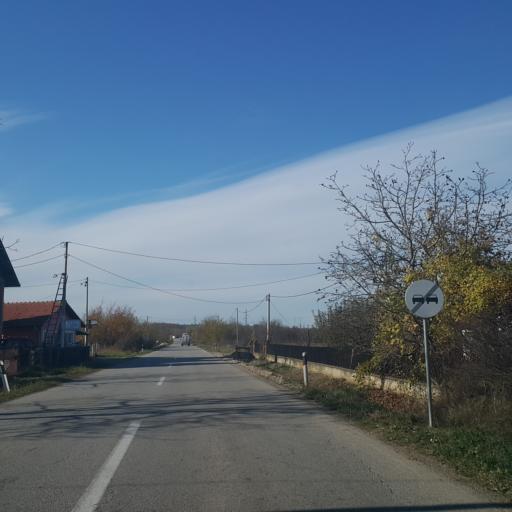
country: RS
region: Central Serbia
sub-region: Sumadijski Okrug
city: Topola
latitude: 44.2508
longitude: 20.7615
